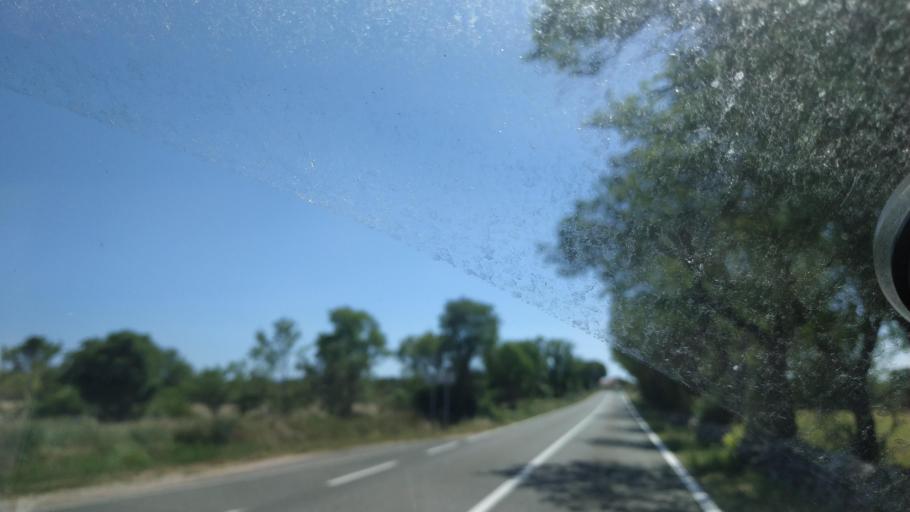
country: HR
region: Sibensko-Kniniska
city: Drnis
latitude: 43.8170
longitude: 16.0562
